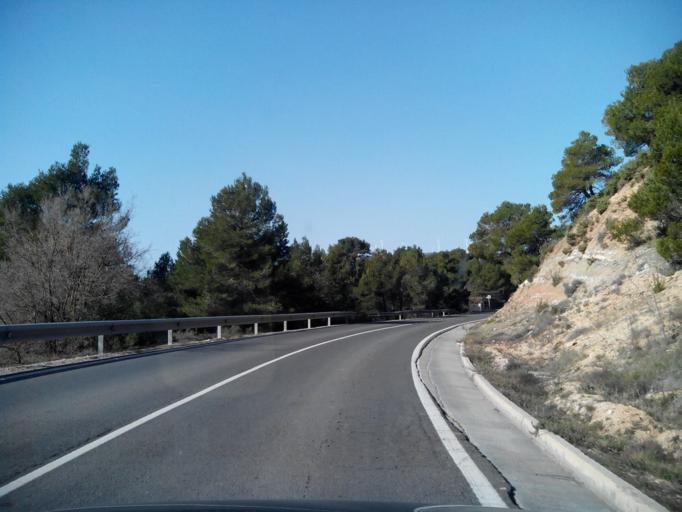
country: ES
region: Catalonia
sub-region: Provincia de Tarragona
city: Conesa
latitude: 41.4864
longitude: 1.3118
